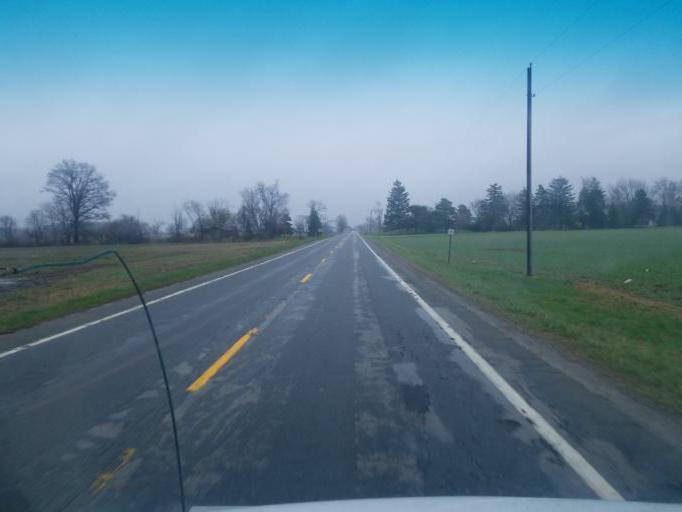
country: US
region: Ohio
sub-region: Wood County
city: Weston
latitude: 41.3722
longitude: -83.7299
